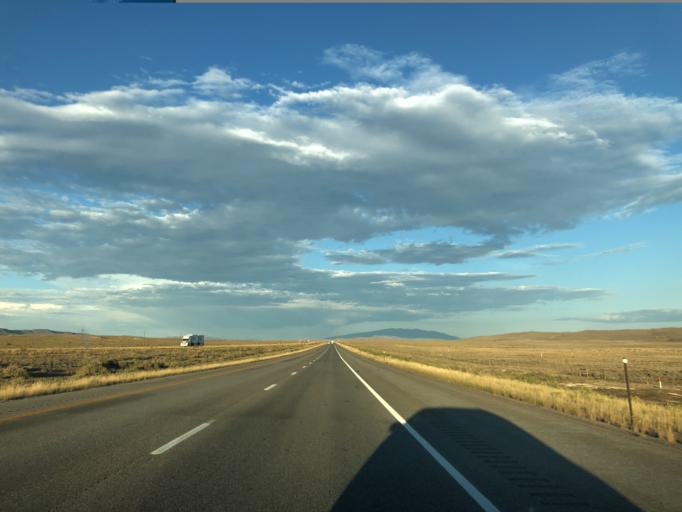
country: US
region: Wyoming
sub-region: Carbon County
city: Rawlins
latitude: 41.7681
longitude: -107.0419
